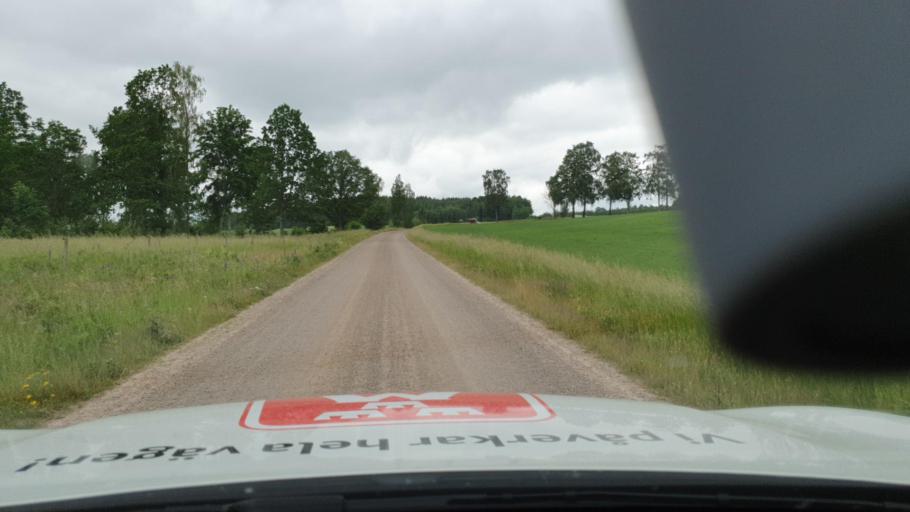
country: SE
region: Vaestra Goetaland
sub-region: Hjo Kommun
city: Hjo
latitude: 58.3513
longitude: 14.3326
